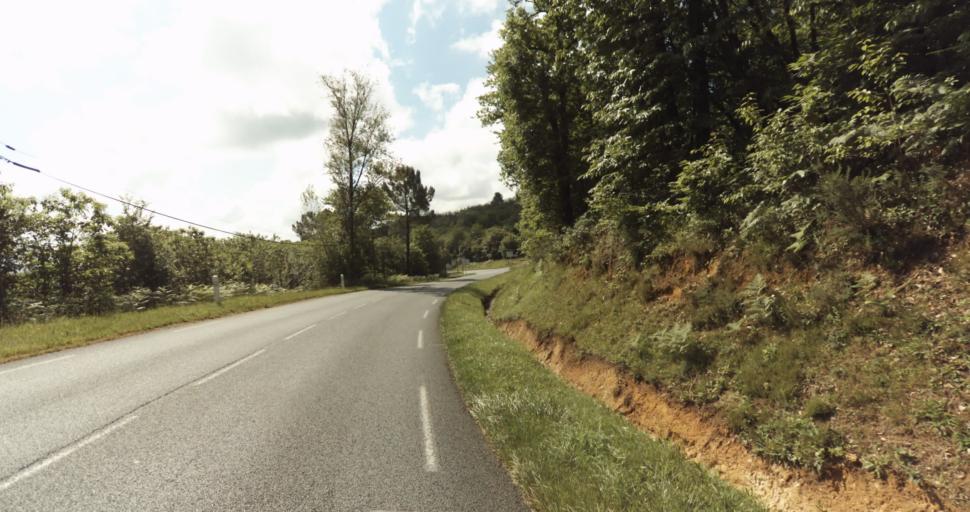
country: FR
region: Aquitaine
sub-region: Departement de la Dordogne
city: Le Bugue
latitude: 44.8425
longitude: 0.8757
